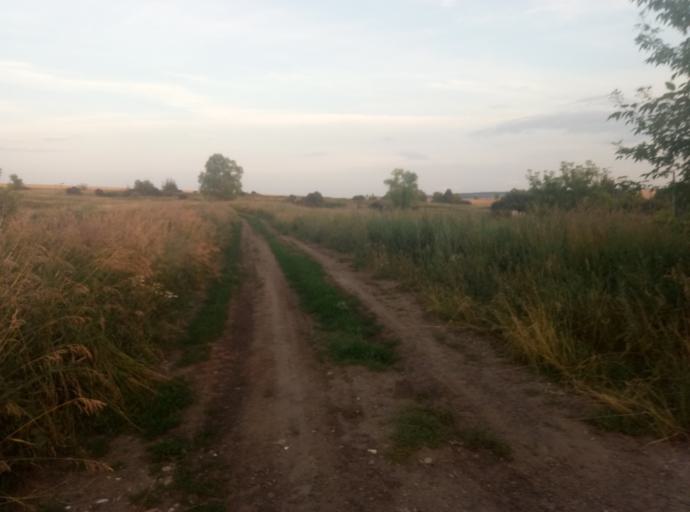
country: RU
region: Tula
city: Kireyevsk
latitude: 53.7991
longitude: 37.8645
